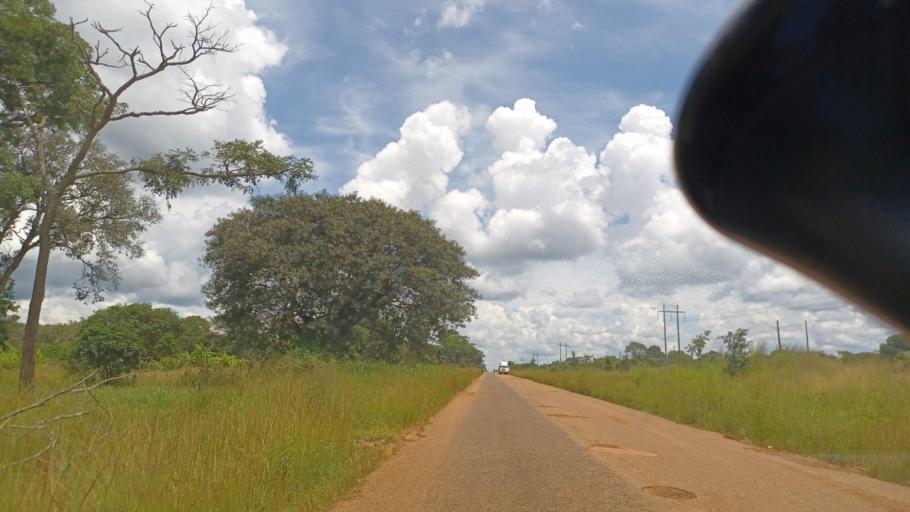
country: ZM
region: North-Western
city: Solwezi
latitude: -12.4897
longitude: 26.1909
